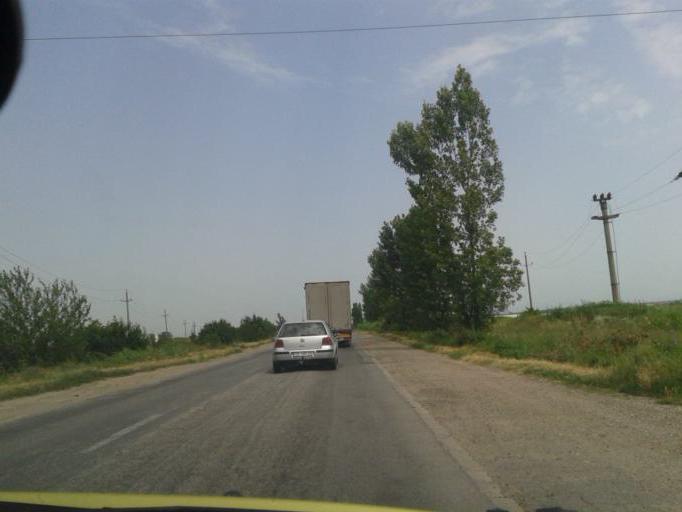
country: RO
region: Dambovita
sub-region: Oras Gaesti
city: Gaesti
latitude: 44.6923
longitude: 25.3126
